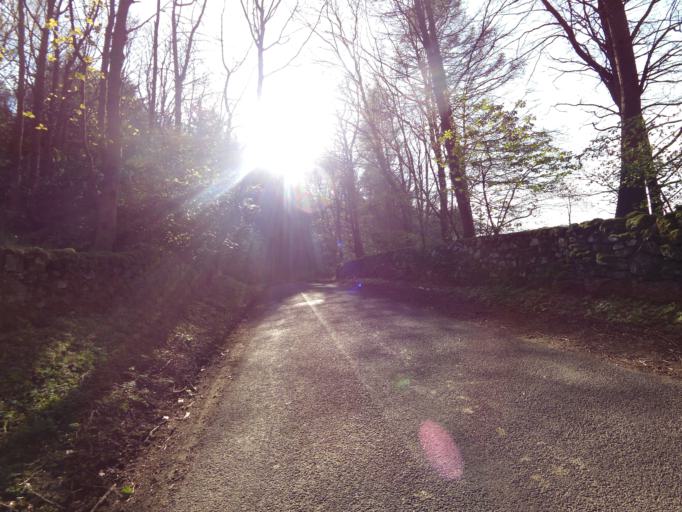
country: GB
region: Scotland
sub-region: Fife
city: Falkland
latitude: 56.2502
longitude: -3.2179
